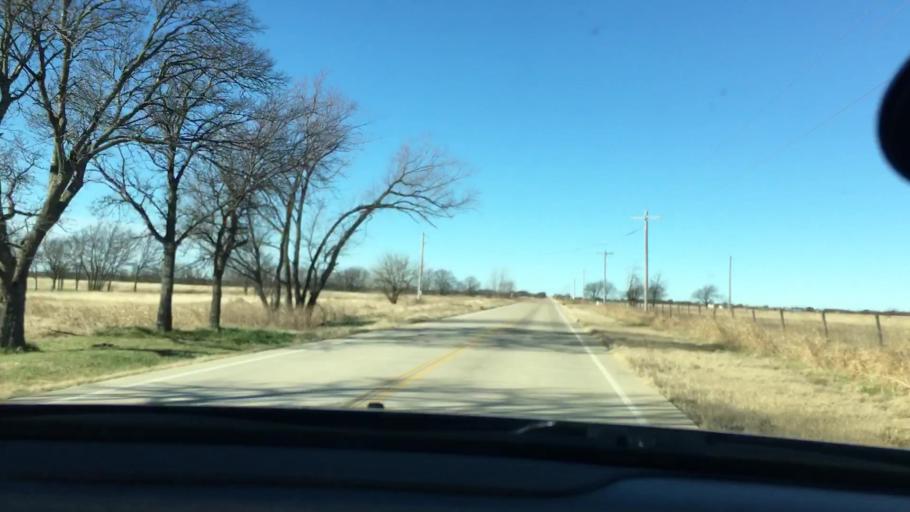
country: US
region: Oklahoma
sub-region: Marshall County
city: Madill
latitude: 34.1145
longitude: -96.6893
